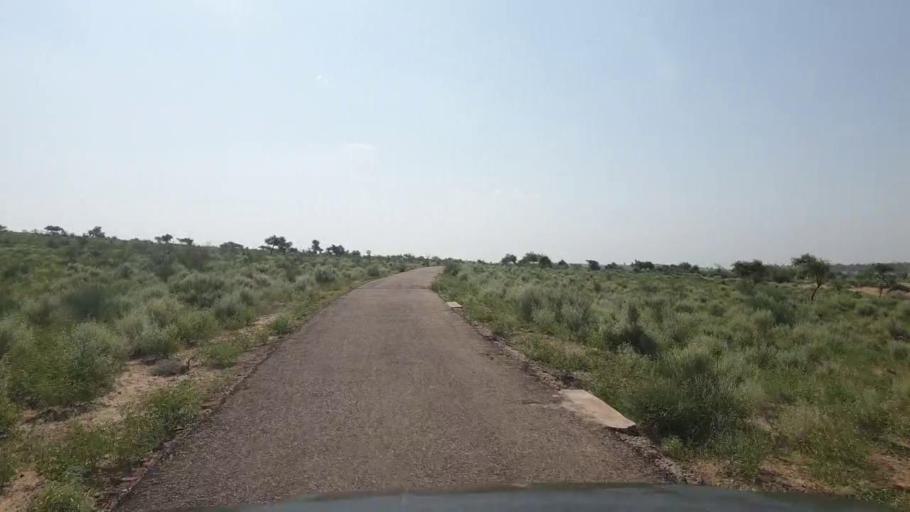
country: PK
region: Sindh
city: Islamkot
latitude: 25.1772
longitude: 70.3957
